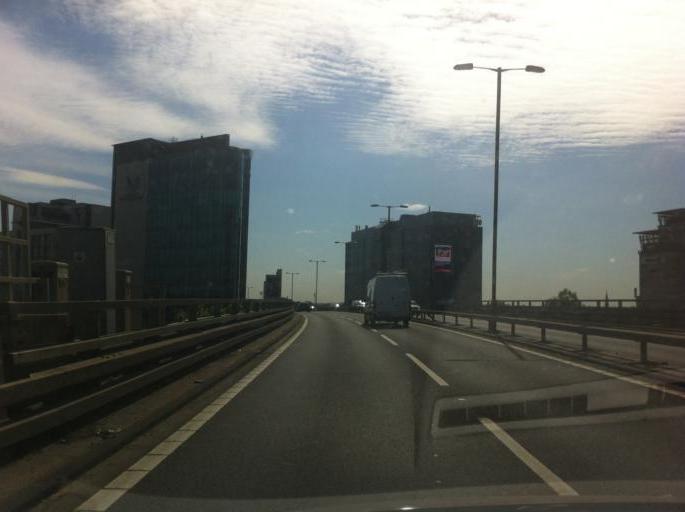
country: GB
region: England
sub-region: Greater London
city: Brentford
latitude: 51.4895
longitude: -0.3164
